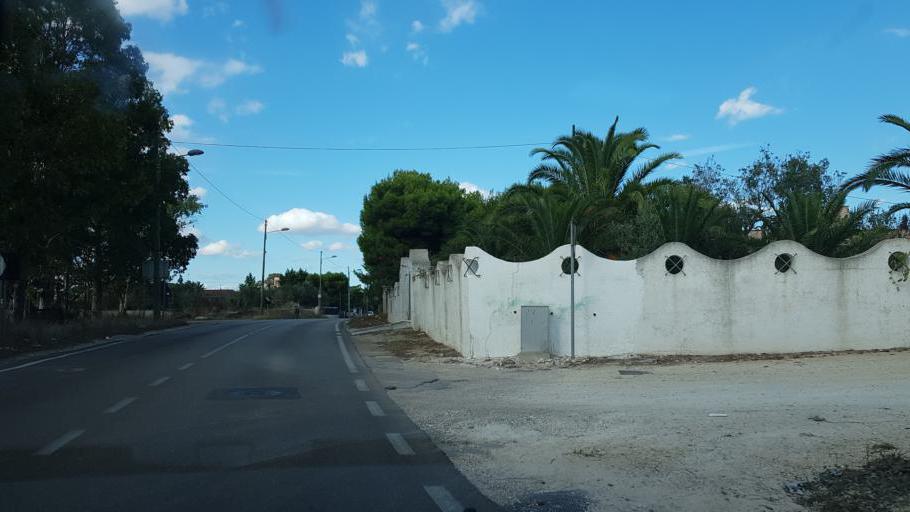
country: IT
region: Apulia
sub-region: Provincia di Lecce
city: Nardo
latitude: 40.1504
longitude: 18.0180
